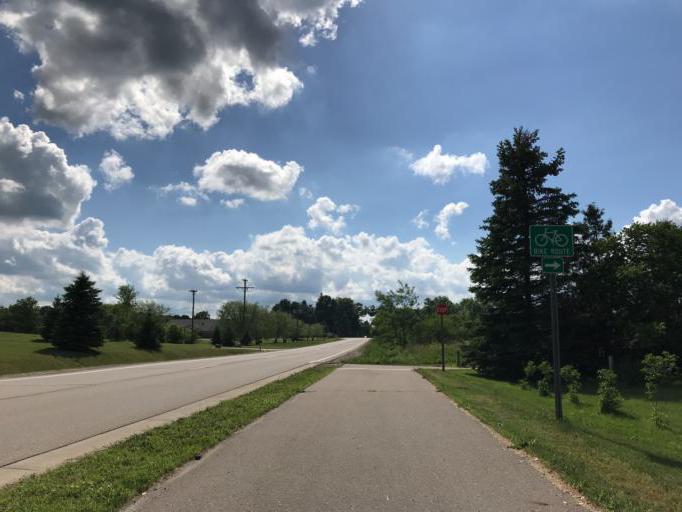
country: US
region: Michigan
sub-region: Oakland County
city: South Lyon
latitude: 42.4314
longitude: -83.6587
